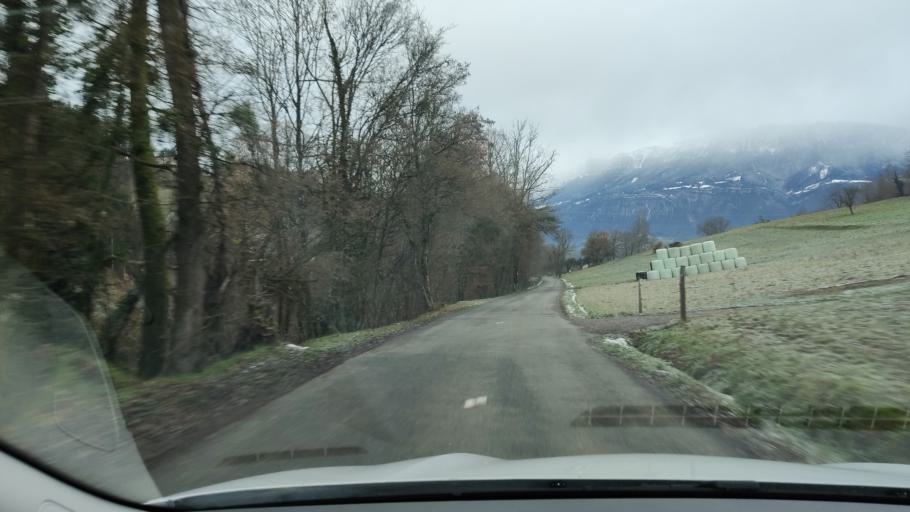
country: FR
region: Rhone-Alpes
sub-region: Departement de la Savoie
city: Montmelian
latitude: 45.4535
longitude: 6.0589
